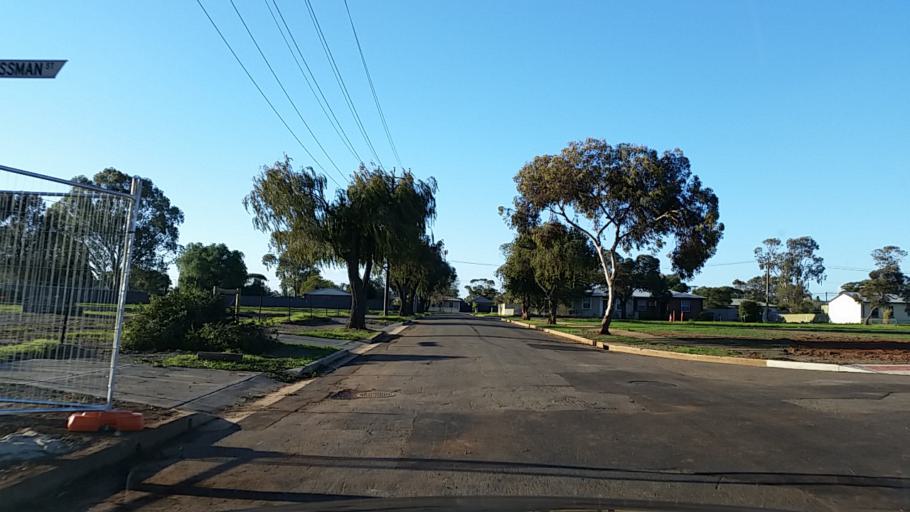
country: AU
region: South Australia
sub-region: Playford
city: Smithfield
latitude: -34.6817
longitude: 138.6683
